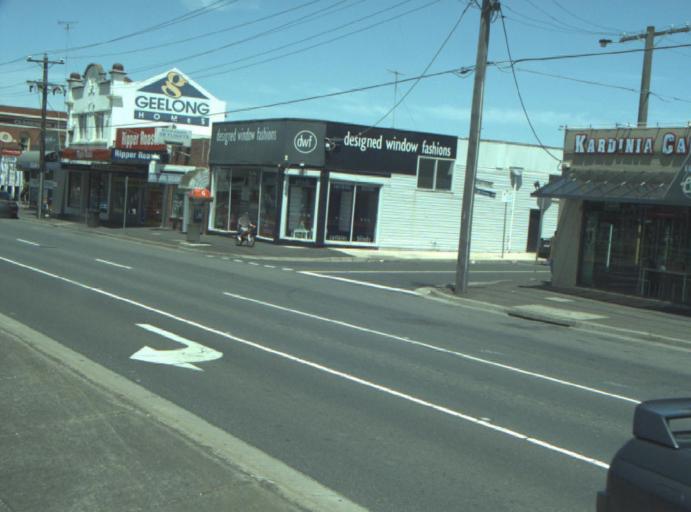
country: AU
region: Victoria
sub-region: Greater Geelong
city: Geelong
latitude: -38.1550
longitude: 144.3513
